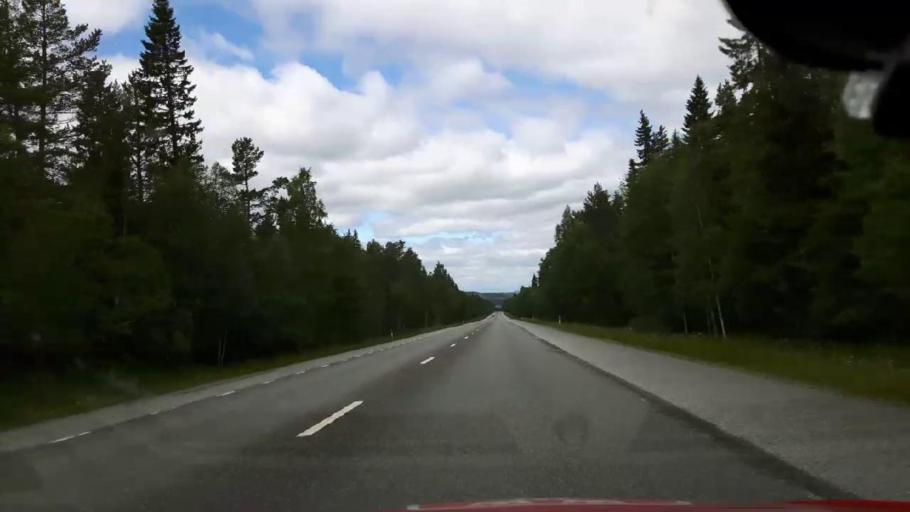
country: SE
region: Jaemtland
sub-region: Braecke Kommun
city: Braecke
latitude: 62.7059
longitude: 15.4959
